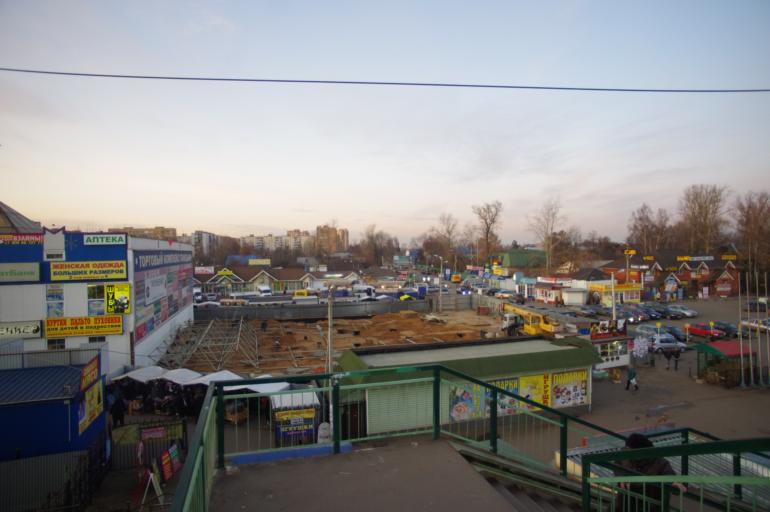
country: RU
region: Moskovskaya
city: Golitsyno
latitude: 55.6156
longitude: 36.9869
